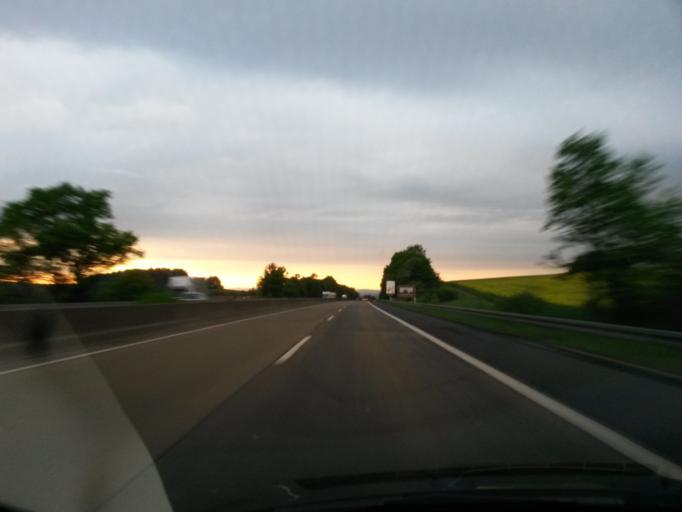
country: DE
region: Hesse
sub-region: Regierungsbezirk Kassel
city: Eichenzell
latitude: 50.4656
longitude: 9.7181
